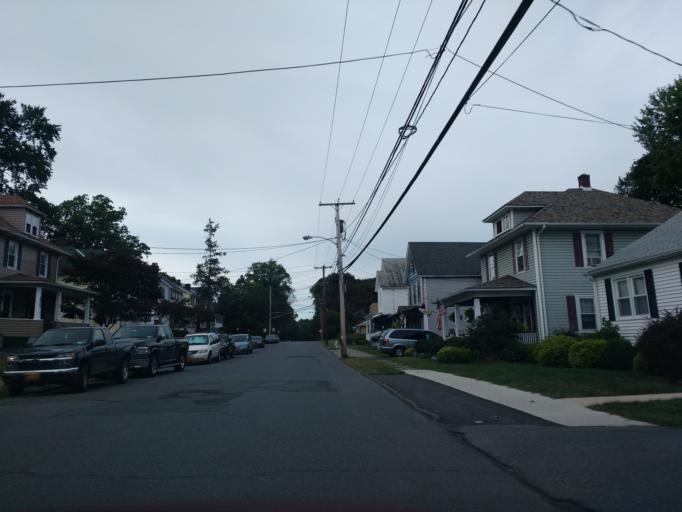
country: US
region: New York
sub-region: Ulster County
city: Kingston
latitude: 41.9247
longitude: -74.0000
